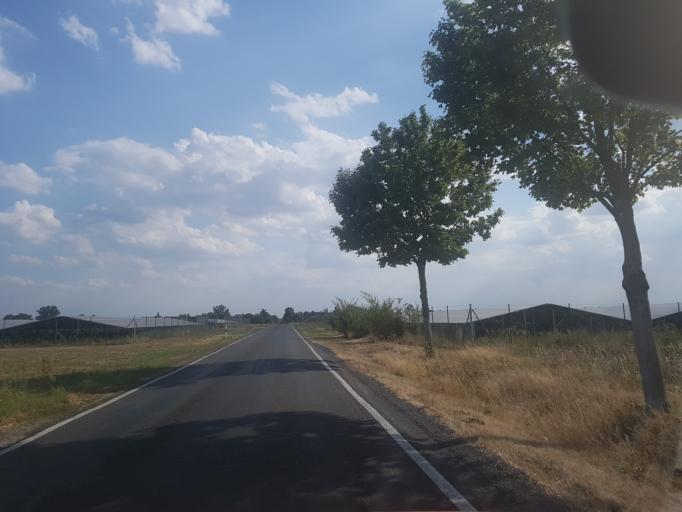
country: DE
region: Saxony-Anhalt
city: Holzdorf
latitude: 51.7812
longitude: 13.2143
